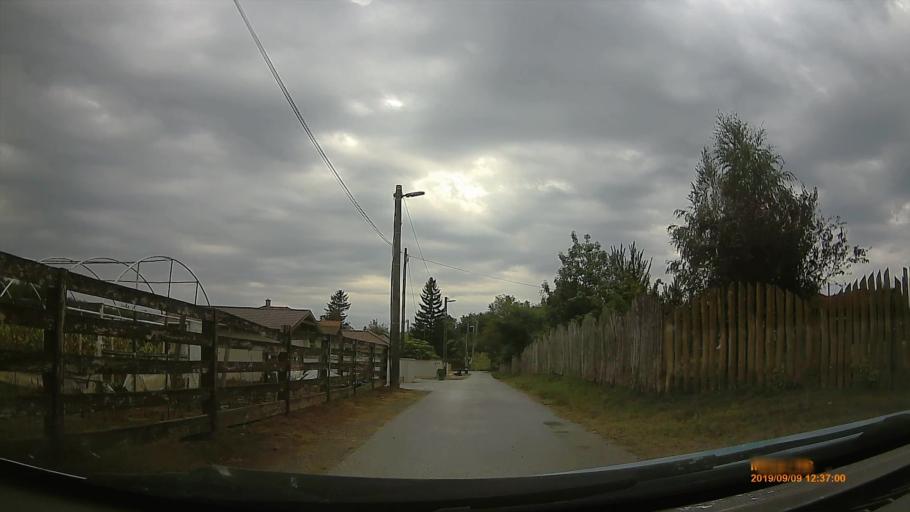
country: HU
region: Szabolcs-Szatmar-Bereg
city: Nyirpazony
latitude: 47.9967
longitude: 21.8081
